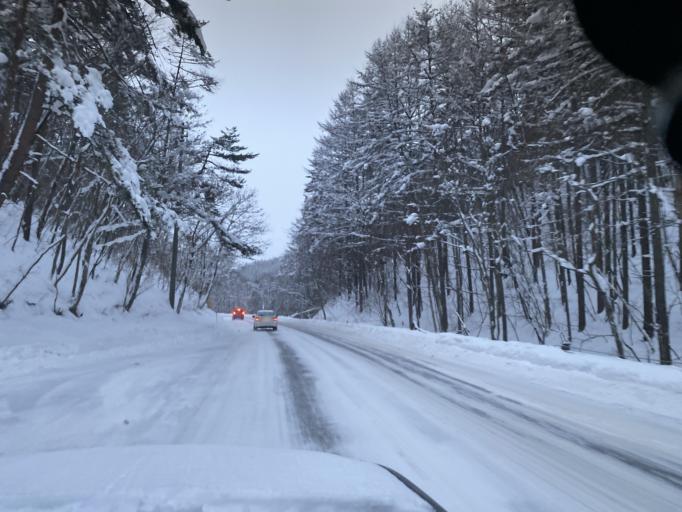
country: JP
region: Nagano
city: Omachi
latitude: 36.5469
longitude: 137.8630
